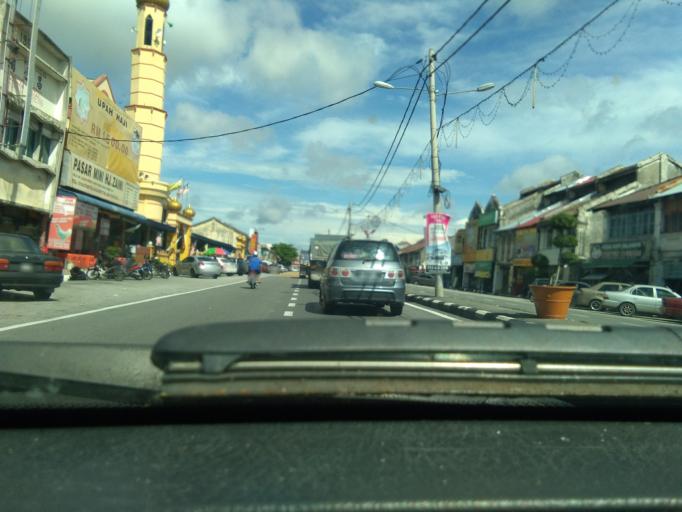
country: MY
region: Perak
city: Bagan Serai
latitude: 5.0099
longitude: 100.5367
